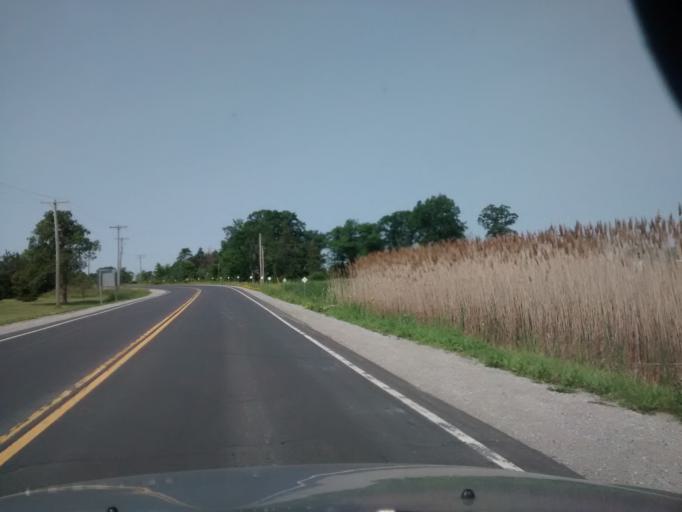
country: CA
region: Ontario
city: Hamilton
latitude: 42.9702
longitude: -79.7711
